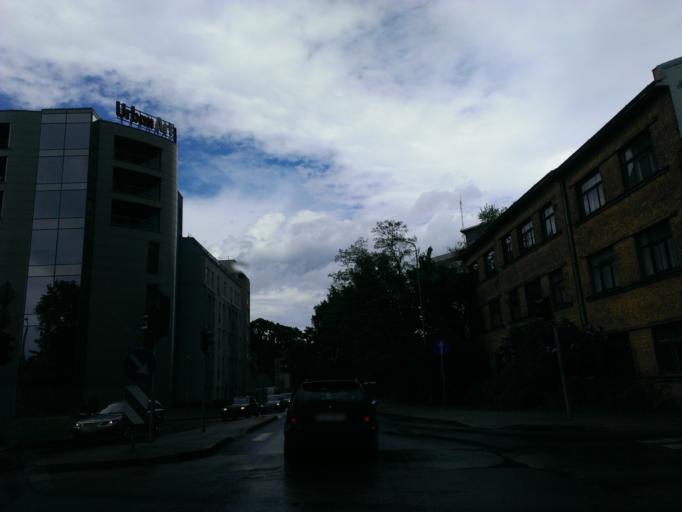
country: LV
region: Riga
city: Riga
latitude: 56.9203
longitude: 24.0976
